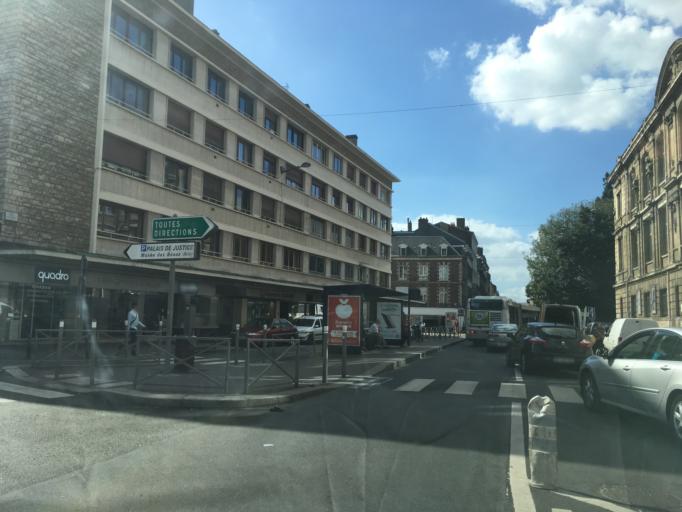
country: FR
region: Haute-Normandie
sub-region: Departement de la Seine-Maritime
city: Rouen
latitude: 49.4442
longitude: 1.0947
